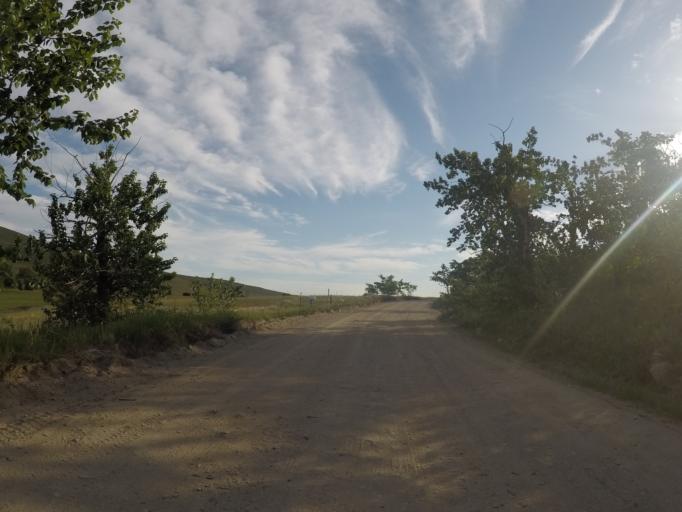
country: US
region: Montana
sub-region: Stillwater County
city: Absarokee
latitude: 45.2973
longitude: -109.5326
